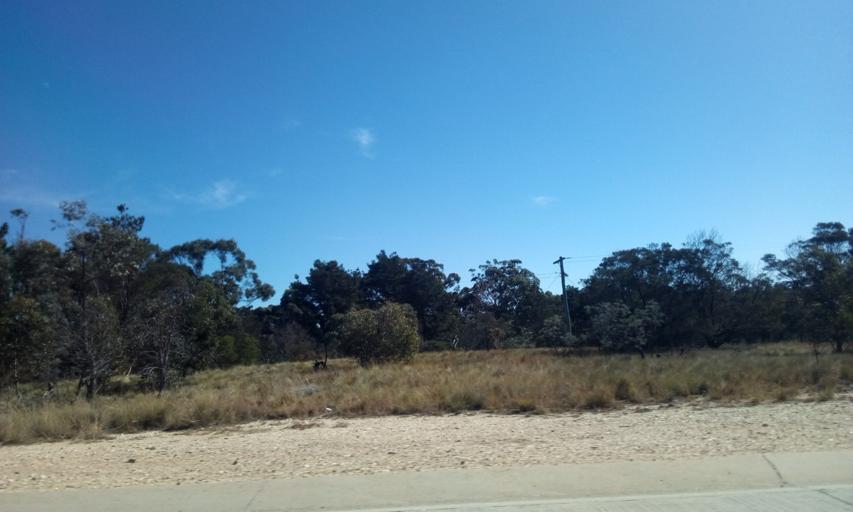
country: AU
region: New South Wales
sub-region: Yass Valley
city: Gundaroo
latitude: -35.1015
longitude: 149.3740
